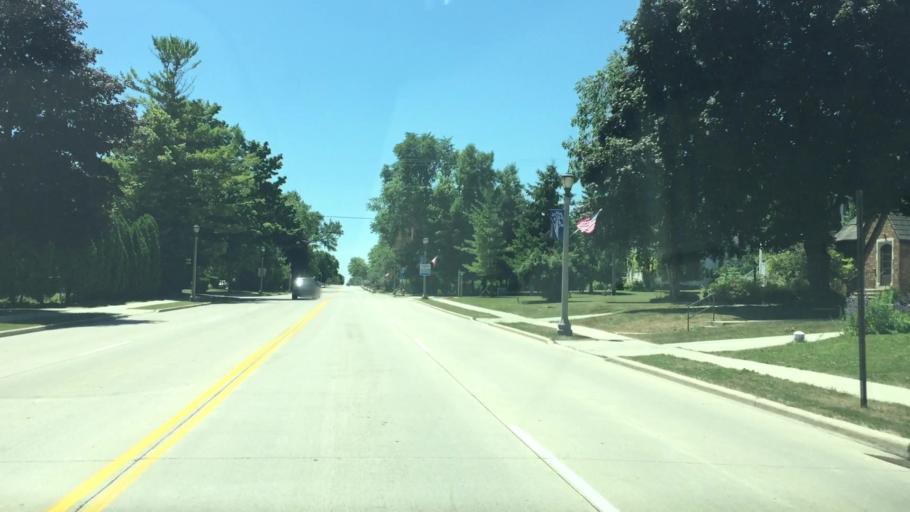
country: US
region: Wisconsin
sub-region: Calumet County
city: Chilton
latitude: 44.0341
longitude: -88.1629
